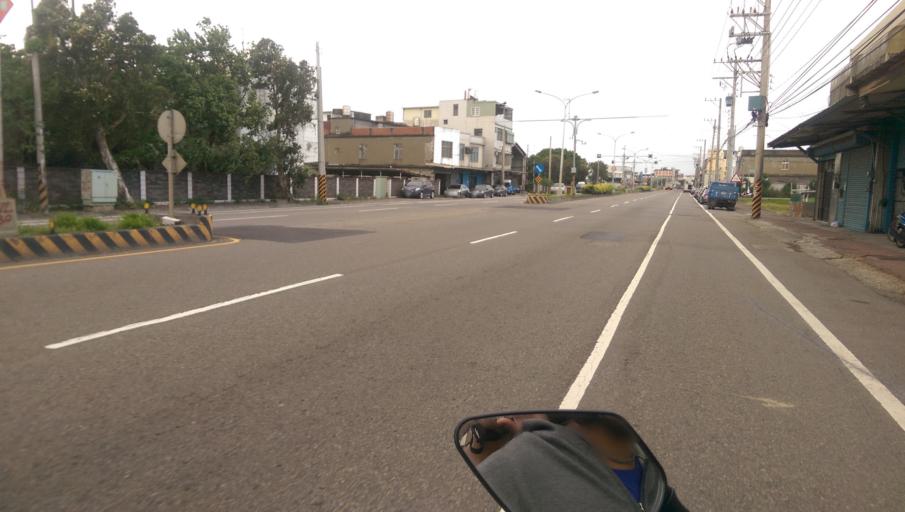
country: TW
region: Taiwan
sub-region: Hsinchu
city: Hsinchu
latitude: 24.8222
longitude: 120.9272
